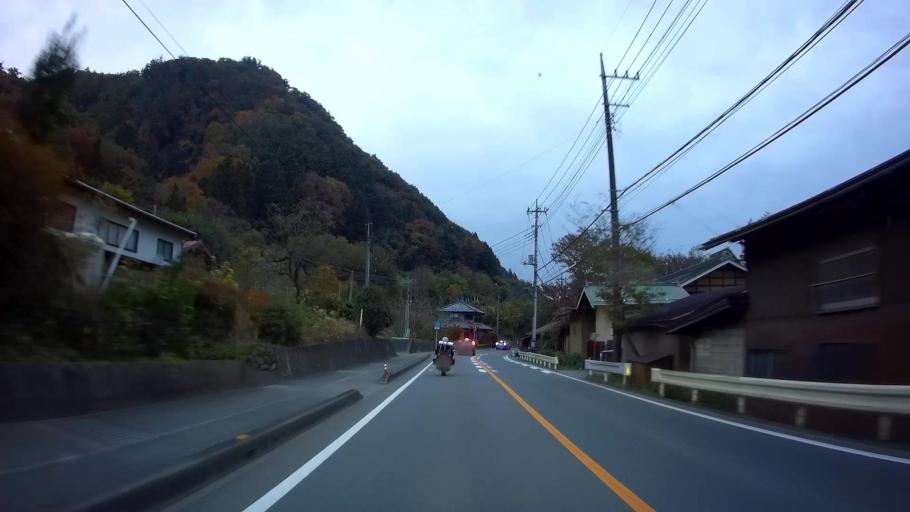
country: JP
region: Gunma
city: Nakanojomachi
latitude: 36.5548
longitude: 138.7771
